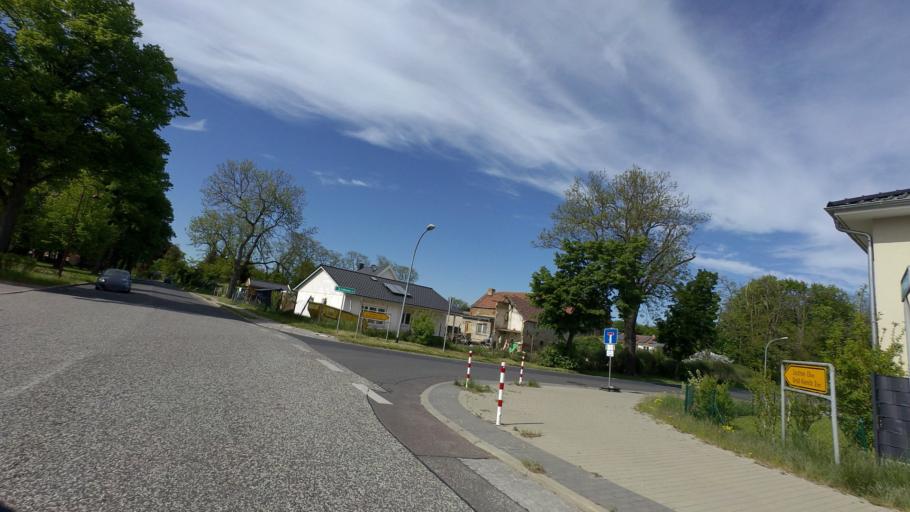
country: DE
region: Brandenburg
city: Rangsdorf
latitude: 52.3197
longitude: 13.4430
